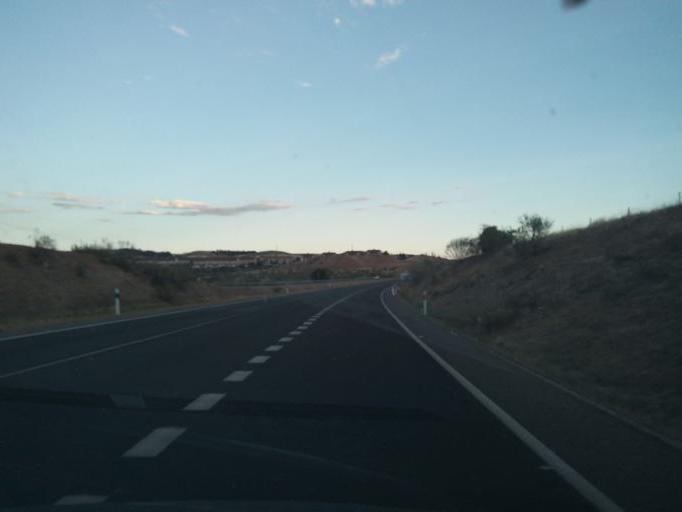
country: ES
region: Madrid
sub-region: Provincia de Madrid
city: Cobena
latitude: 40.5674
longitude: -3.5190
